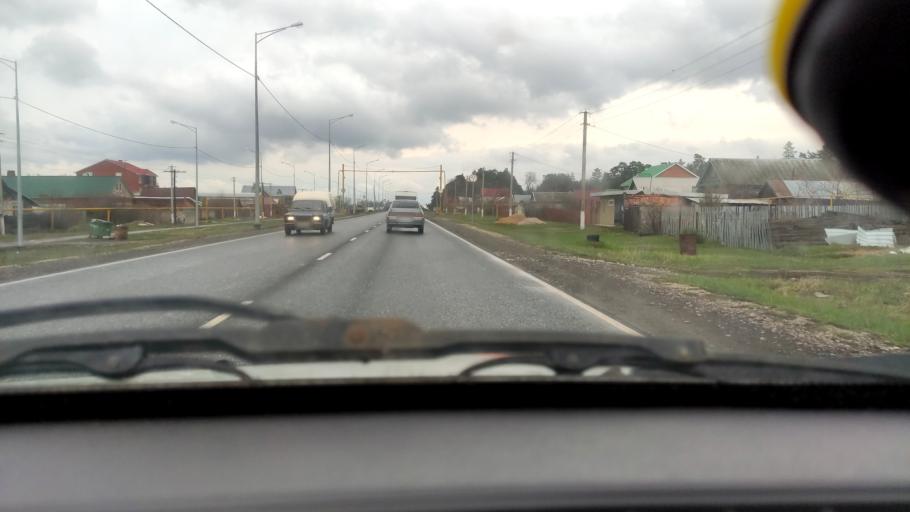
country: RU
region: Samara
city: Povolzhskiy
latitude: 53.5886
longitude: 49.5761
